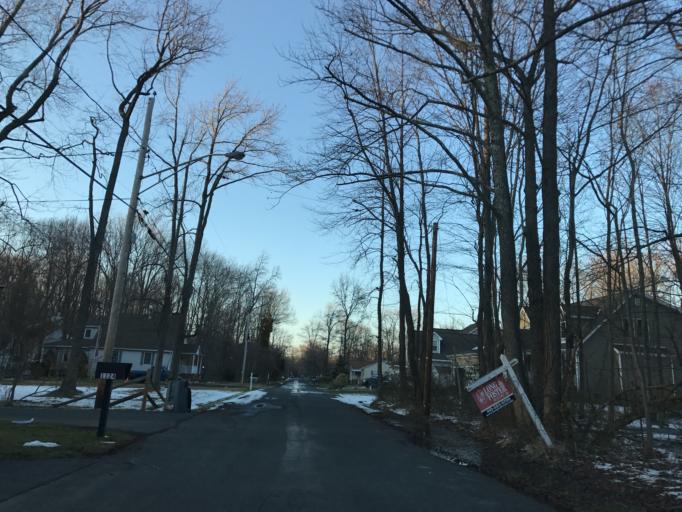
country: US
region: Maryland
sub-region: Baltimore County
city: Edgemere
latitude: 39.2784
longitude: -76.4188
